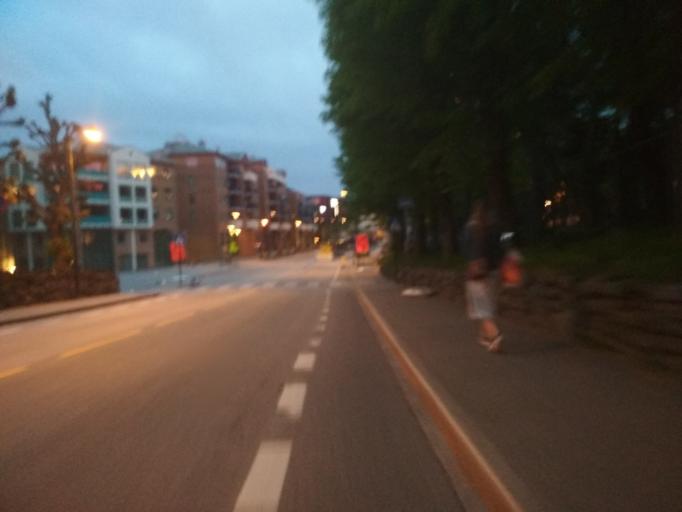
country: NO
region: Rogaland
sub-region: Stavanger
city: Stavanger
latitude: 58.9757
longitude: 5.7188
